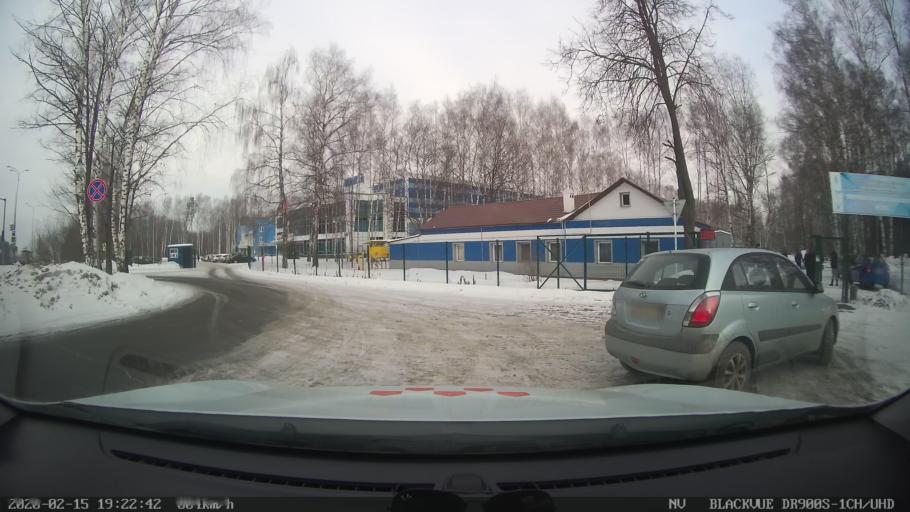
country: RU
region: Tatarstan
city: Osinovo
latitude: 55.8460
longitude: 48.9266
